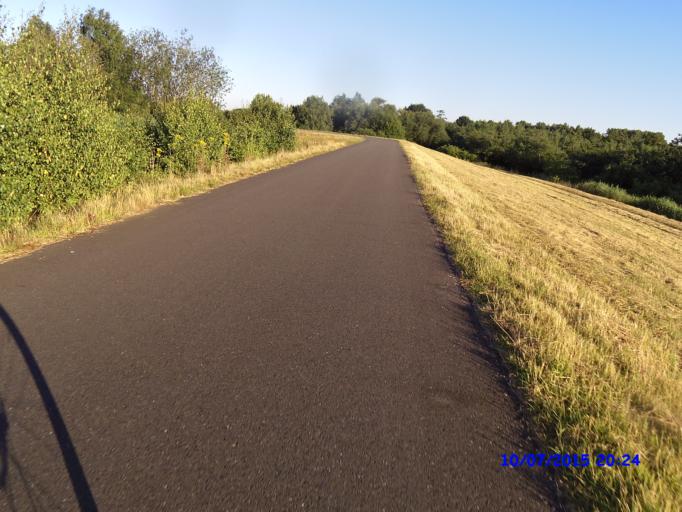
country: BE
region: Flanders
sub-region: Provincie Antwerpen
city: Boom
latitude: 51.0796
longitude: 4.3829
